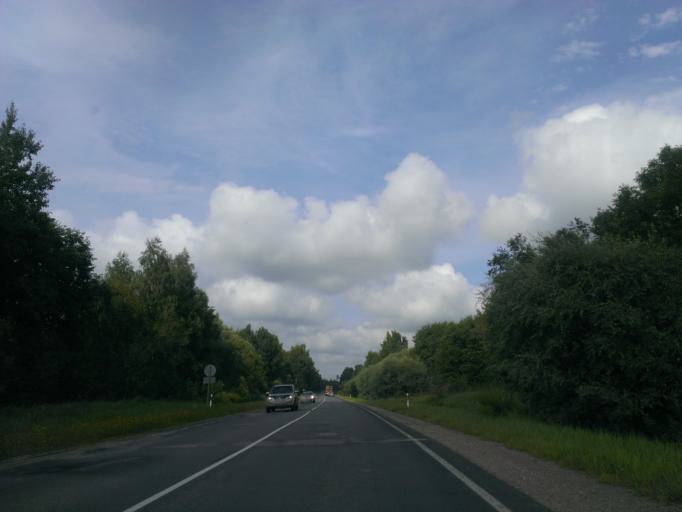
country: LV
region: Amatas Novads
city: Drabesi
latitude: 57.2458
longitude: 25.3299
